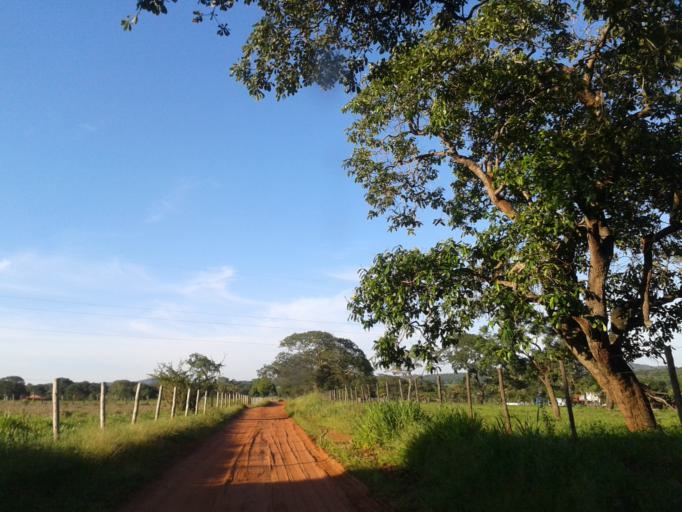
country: BR
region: Minas Gerais
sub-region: Santa Vitoria
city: Santa Vitoria
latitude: -18.9274
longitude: -49.8512
